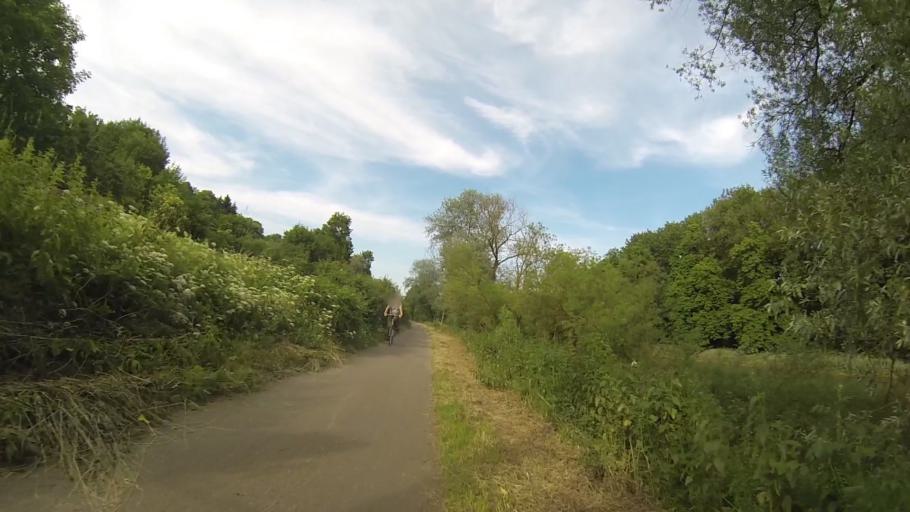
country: DE
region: Baden-Wuerttemberg
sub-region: Tuebingen Region
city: Ulm
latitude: 48.3806
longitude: 9.9696
